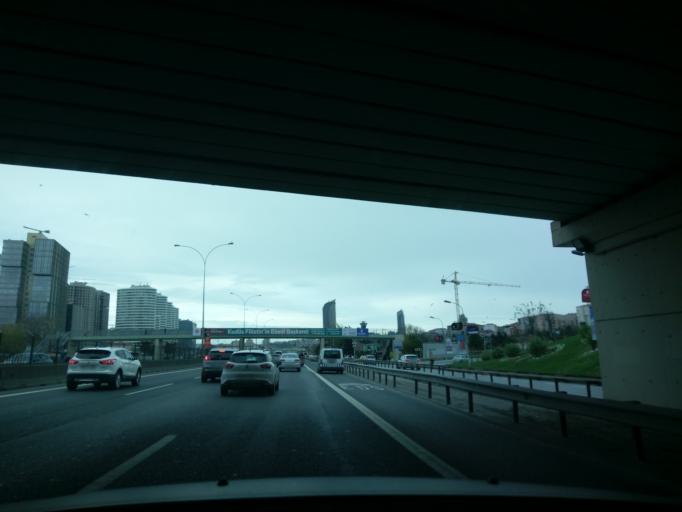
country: TR
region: Istanbul
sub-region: Atasehir
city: Atasehir
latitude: 40.9926
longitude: 29.0734
